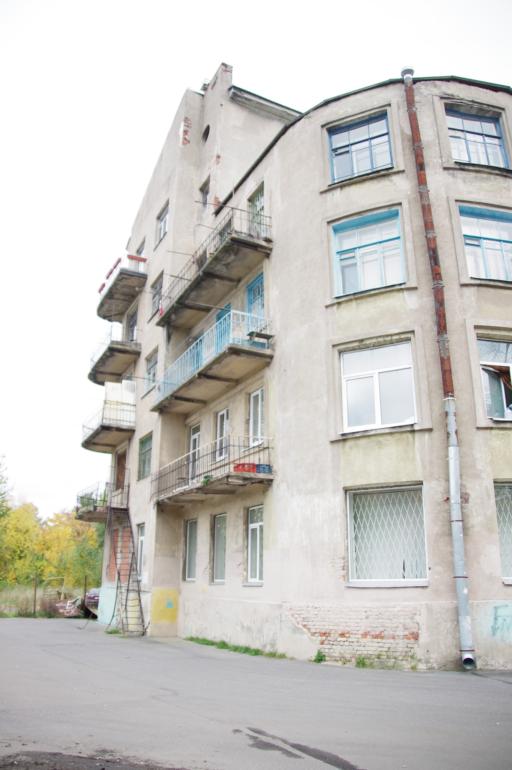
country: RU
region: St.-Petersburg
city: Kronshtadt
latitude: 59.9910
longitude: 29.7705
